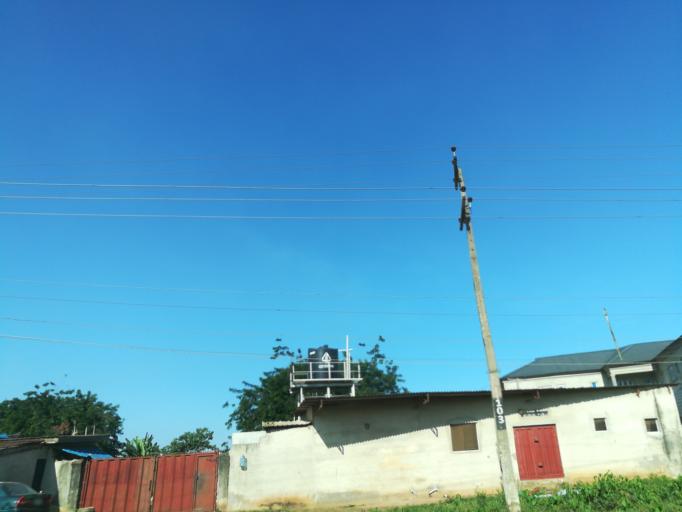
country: NG
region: Lagos
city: Ikorodu
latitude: 6.5791
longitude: 3.5261
